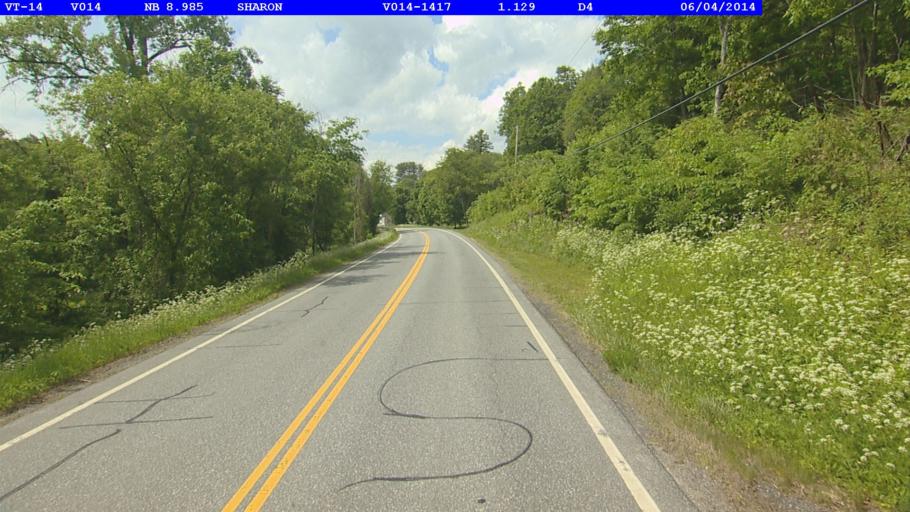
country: US
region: Vermont
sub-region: Windsor County
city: Woodstock
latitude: 43.7359
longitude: -72.4351
